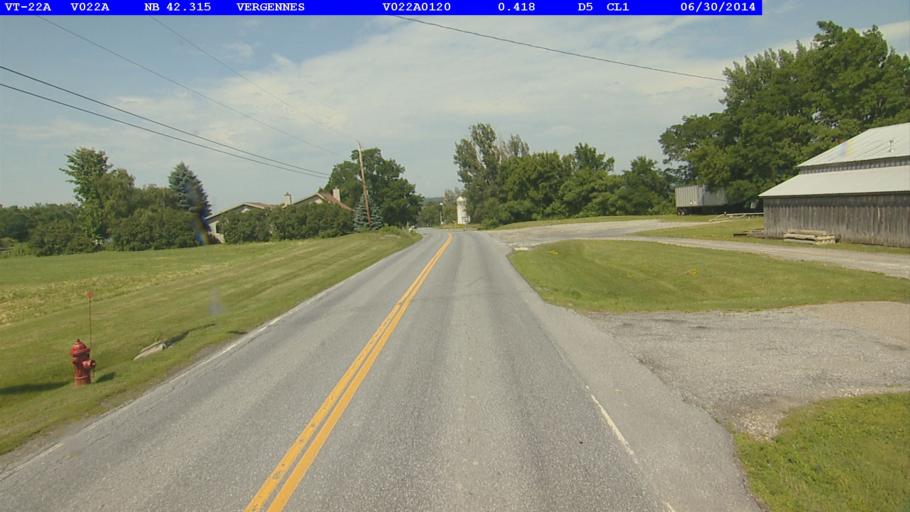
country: US
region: Vermont
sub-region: Addison County
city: Vergennes
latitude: 44.1594
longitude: -73.2629
